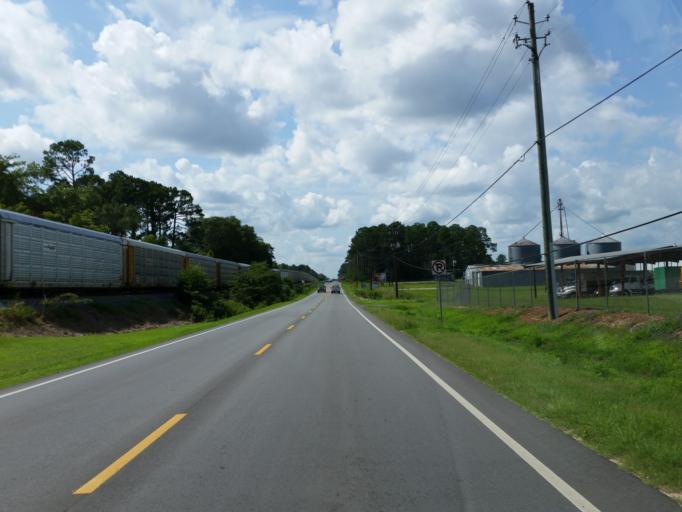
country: US
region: Georgia
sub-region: Turner County
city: Ashburn
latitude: 31.6787
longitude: -83.6397
